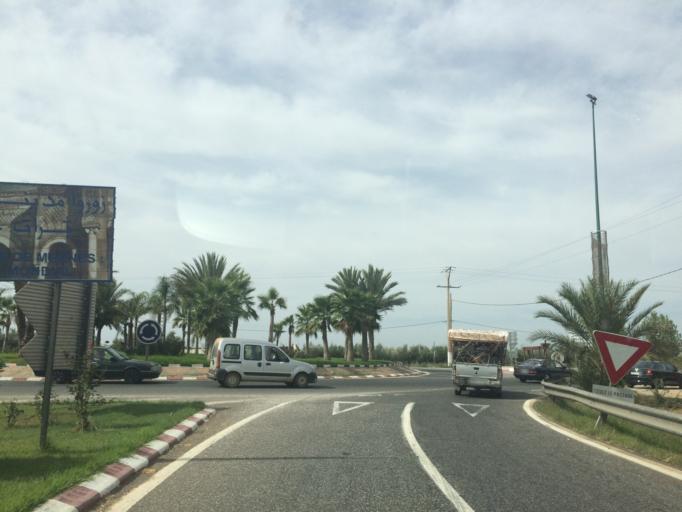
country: MA
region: Meknes-Tafilalet
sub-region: Meknes
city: Meknes
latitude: 33.8339
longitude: -5.5168
